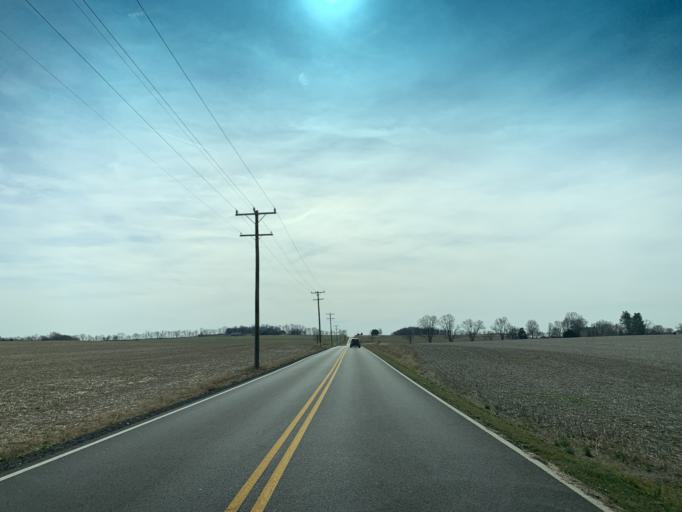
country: US
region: Maryland
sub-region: Frederick County
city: Adamstown
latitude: 39.2727
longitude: -77.4732
